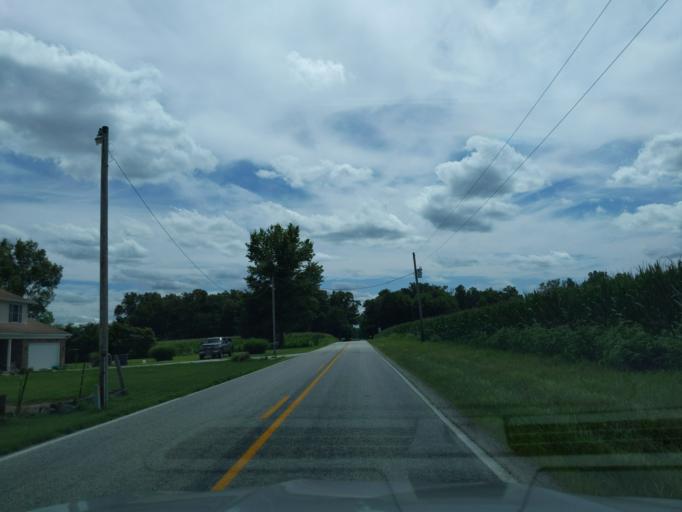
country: US
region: Indiana
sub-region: Ripley County
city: Osgood
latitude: 39.2002
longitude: -85.2776
